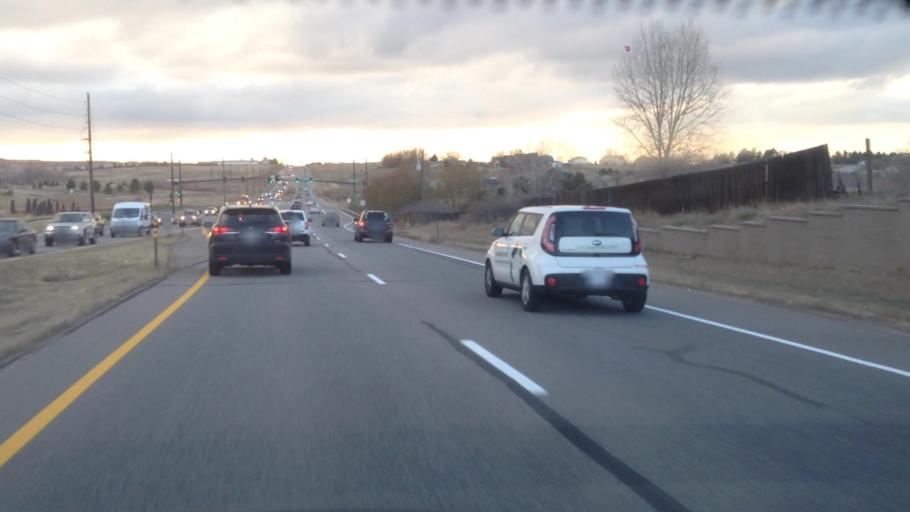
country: US
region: Colorado
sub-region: Douglas County
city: Stonegate
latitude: 39.5364
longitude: -104.8208
